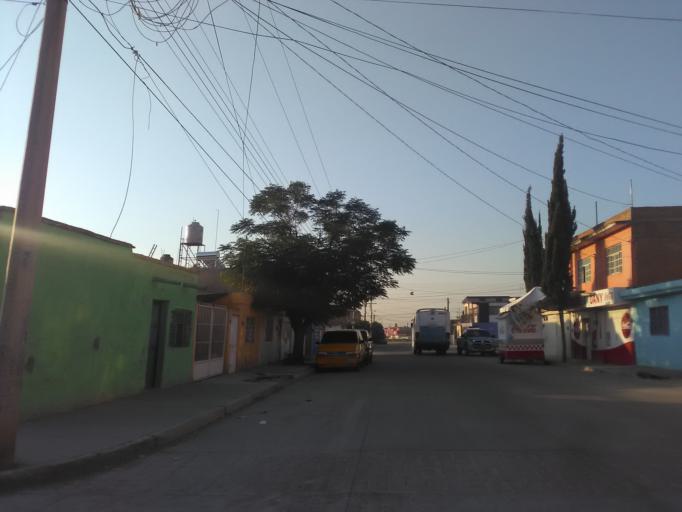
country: MX
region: Durango
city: Victoria de Durango
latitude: 24.0475
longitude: -104.6445
